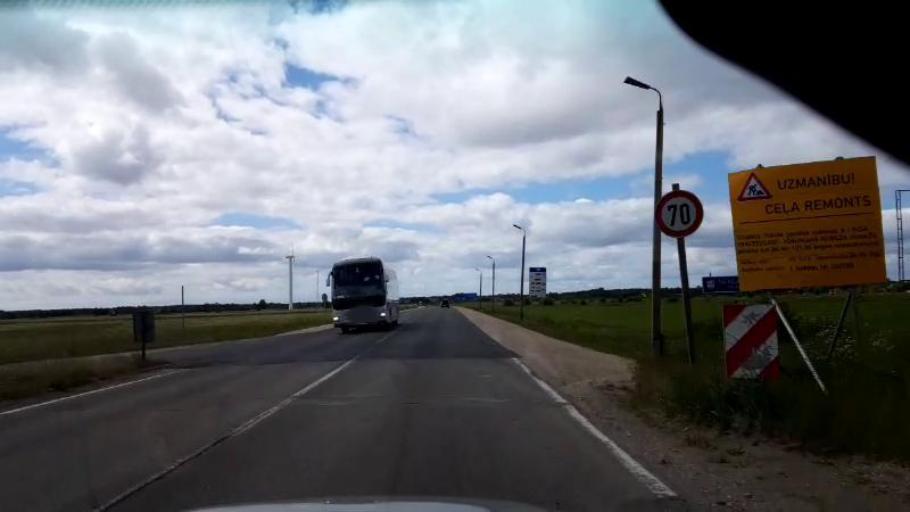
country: LV
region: Salacgrivas
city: Ainazi
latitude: 57.8697
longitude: 24.3758
